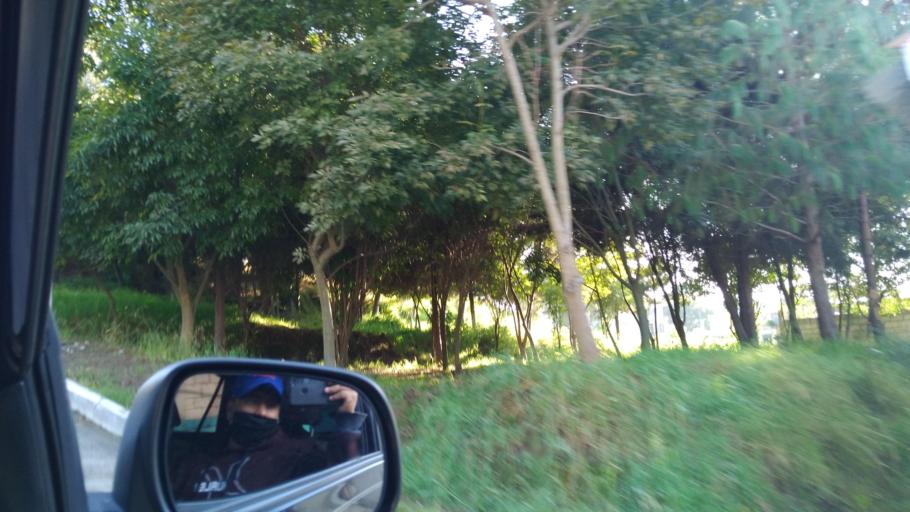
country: GT
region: Quetzaltenango
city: Quetzaltenango
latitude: 14.8531
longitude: -91.5205
